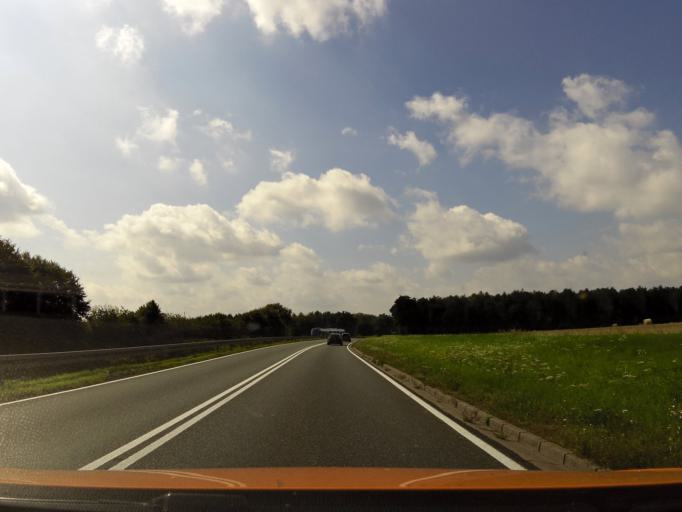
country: PL
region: West Pomeranian Voivodeship
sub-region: Powiat goleniowski
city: Nowogard
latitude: 53.7013
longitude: 15.1680
